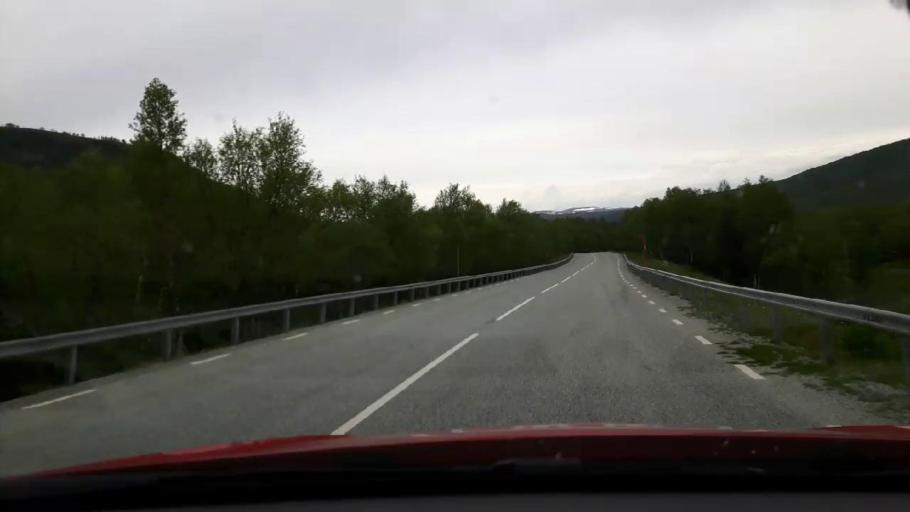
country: NO
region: Sor-Trondelag
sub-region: Tydal
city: Aas
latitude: 62.6834
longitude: 12.4135
